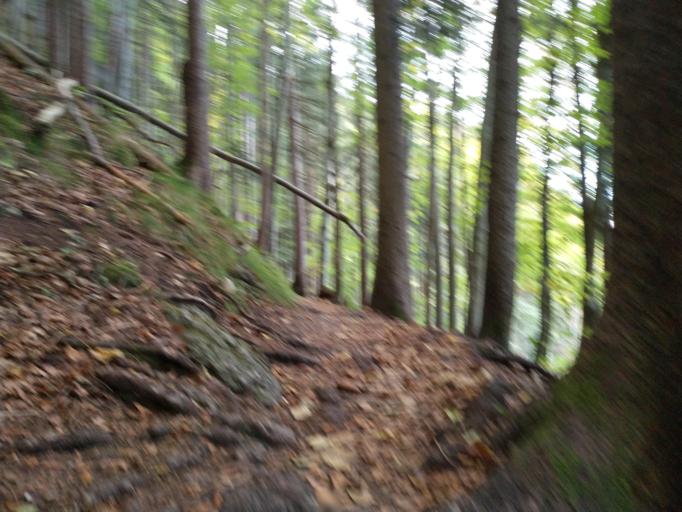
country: AT
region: Tyrol
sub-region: Politischer Bezirk Reutte
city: Vils
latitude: 47.5672
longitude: 10.6336
